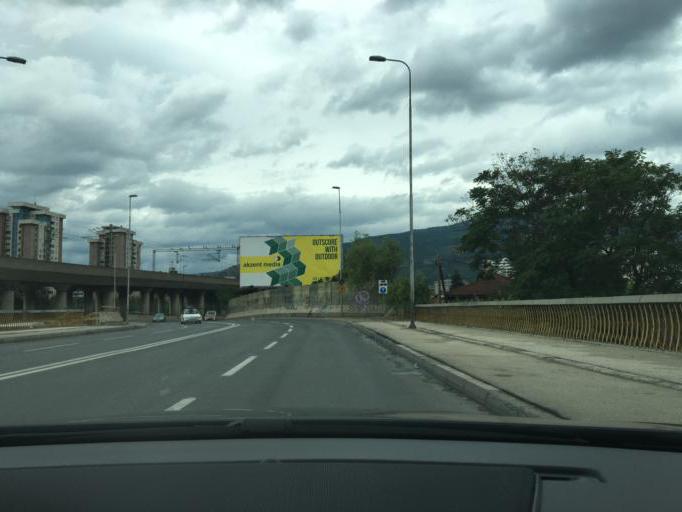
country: MK
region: Karpos
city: Skopje
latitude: 41.9949
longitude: 21.4492
